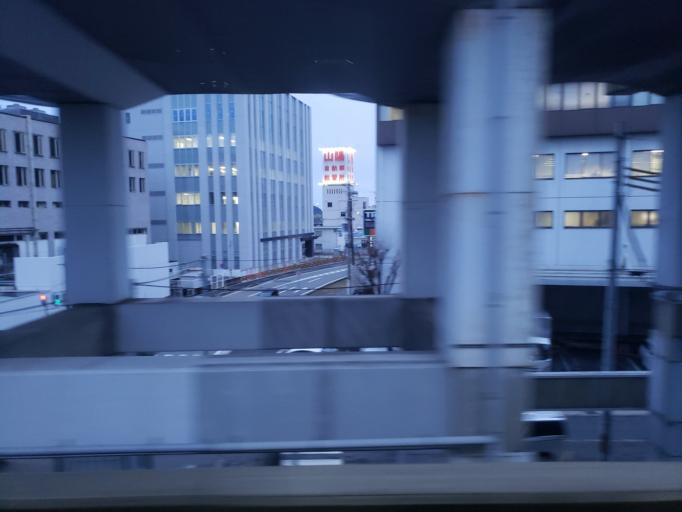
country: JP
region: Hyogo
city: Himeji
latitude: 34.8256
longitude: 134.6986
